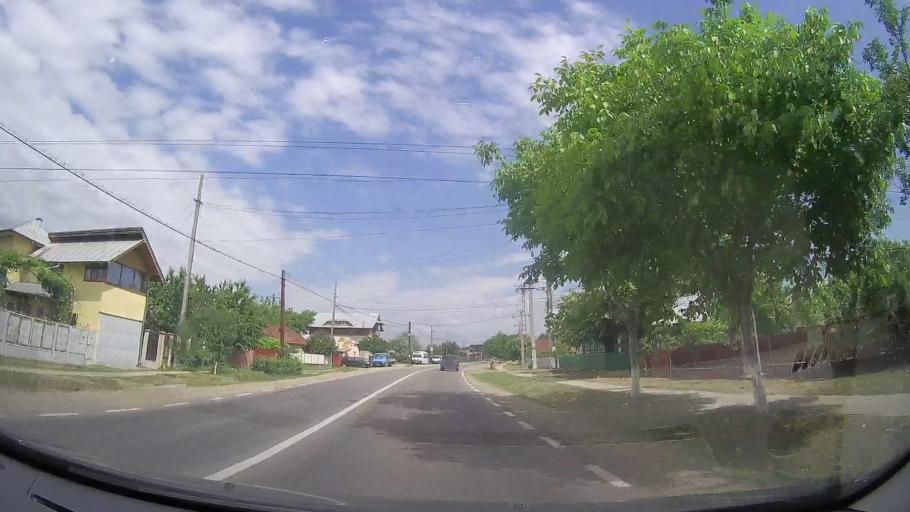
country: RO
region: Prahova
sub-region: Comuna Magurele
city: Magurele
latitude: 45.1030
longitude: 26.0356
